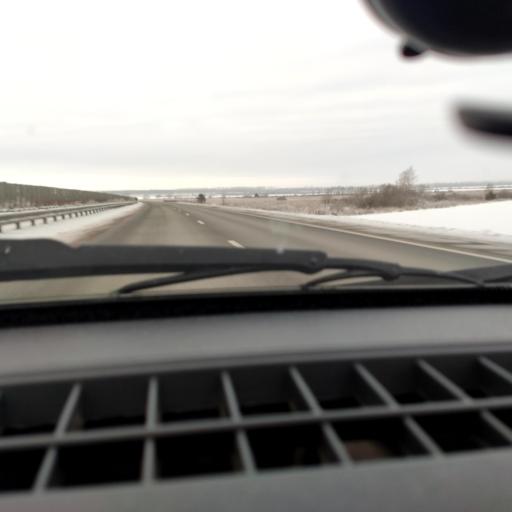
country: RU
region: Bashkortostan
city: Kushnarenkovo
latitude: 55.0660
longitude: 55.3628
